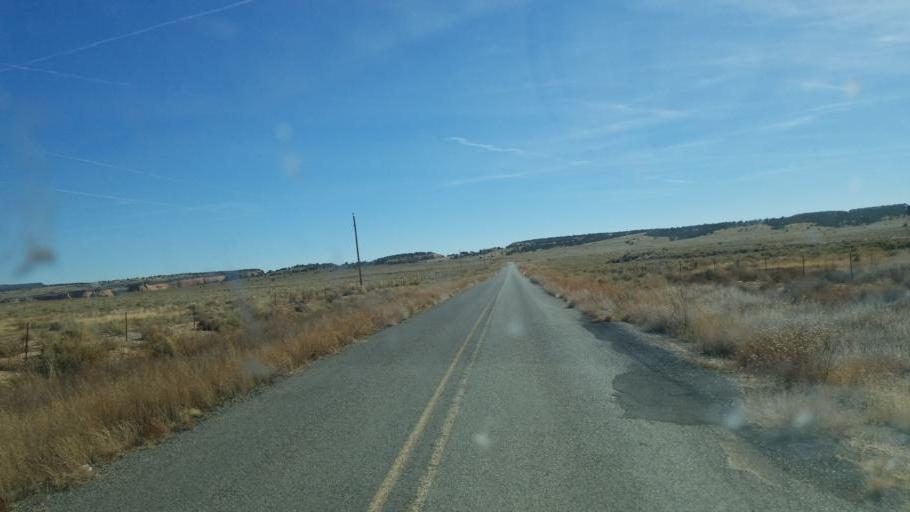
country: US
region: New Mexico
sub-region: McKinley County
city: Thoreau
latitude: 35.4517
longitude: -108.0522
